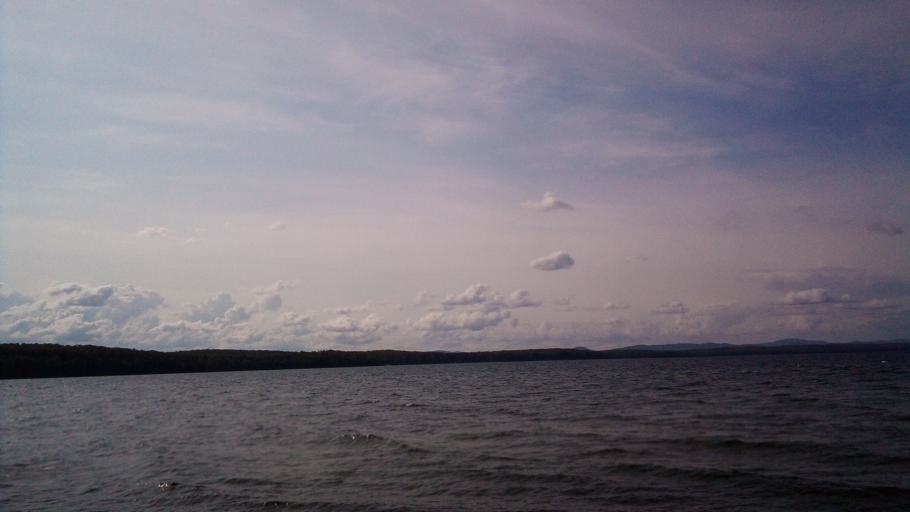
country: RU
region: Chelyabinsk
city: Tayginka
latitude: 55.4760
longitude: 60.4889
